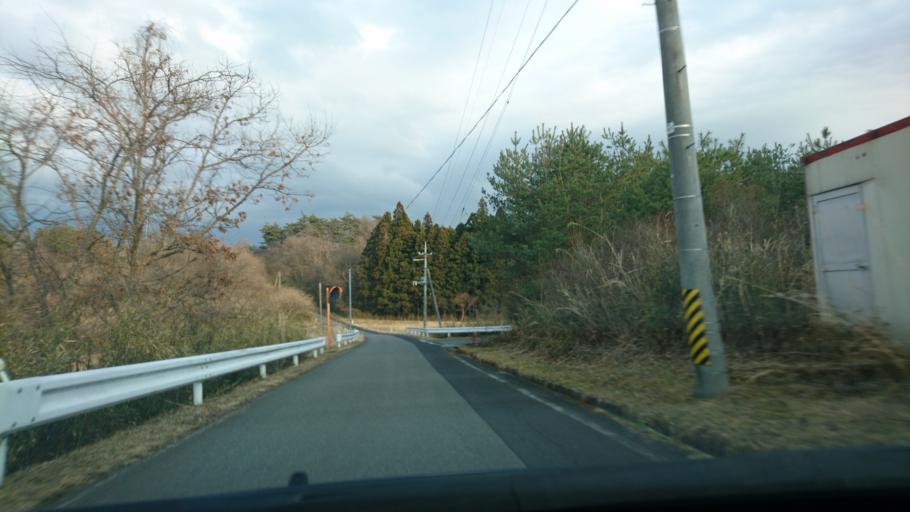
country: JP
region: Iwate
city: Ichinoseki
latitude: 38.8933
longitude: 141.2399
